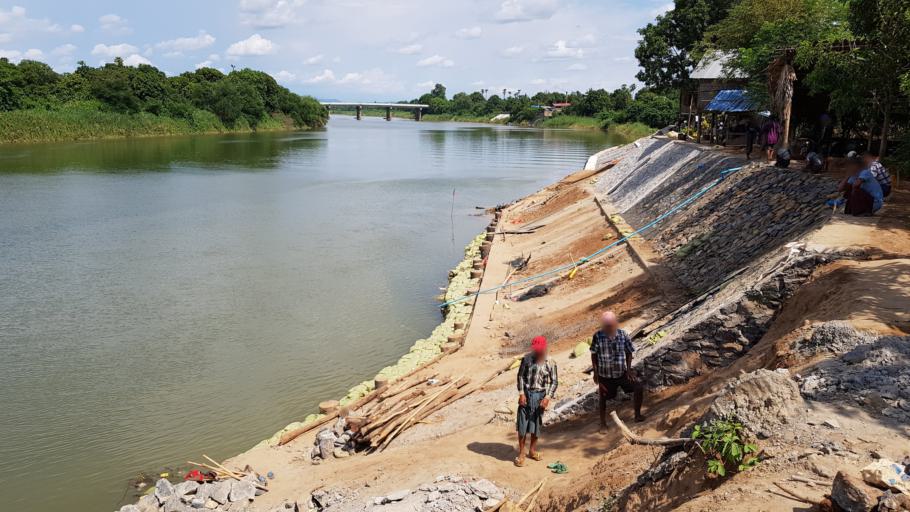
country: MM
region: Sagain
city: Sagaing
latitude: 21.8353
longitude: 95.9850
